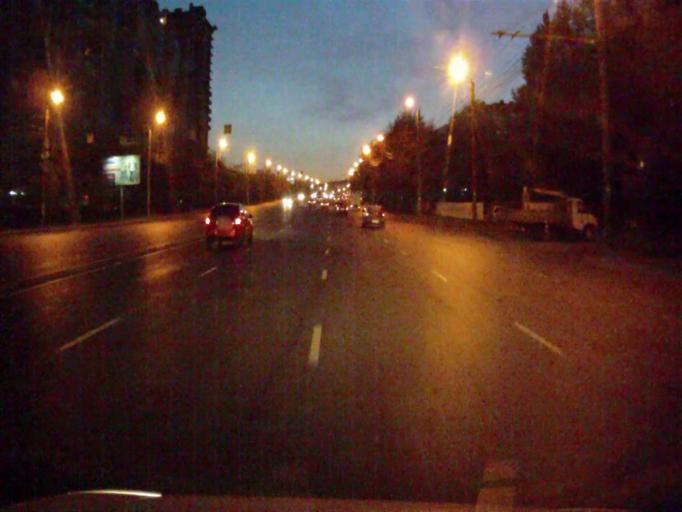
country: RU
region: Chelyabinsk
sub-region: Gorod Chelyabinsk
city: Chelyabinsk
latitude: 55.1787
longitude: 61.3294
